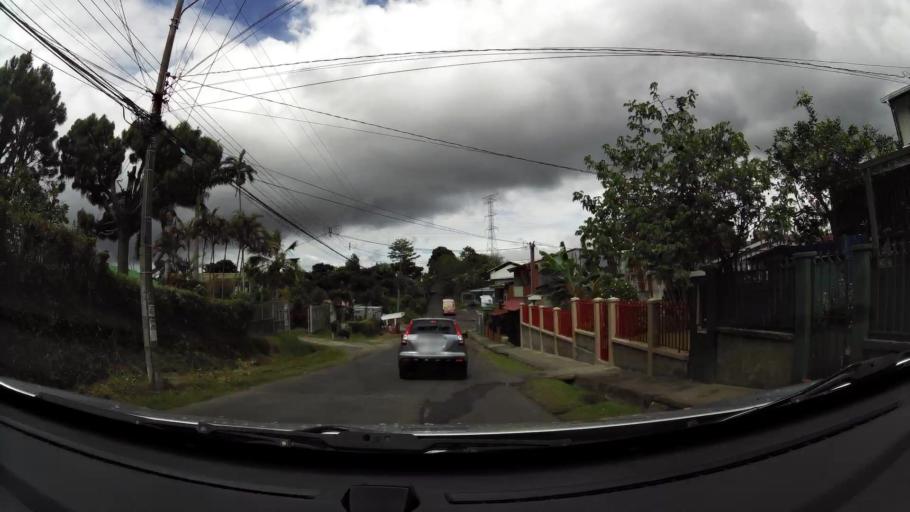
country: CR
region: Cartago
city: Tres Rios
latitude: 9.9174
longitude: -83.9914
